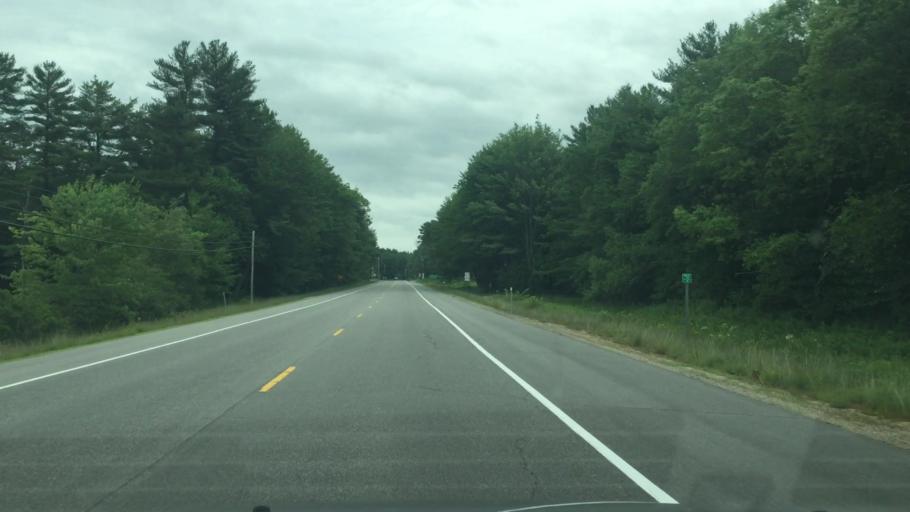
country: US
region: New Hampshire
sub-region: Carroll County
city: Tamworth
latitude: 43.8265
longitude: -71.3326
